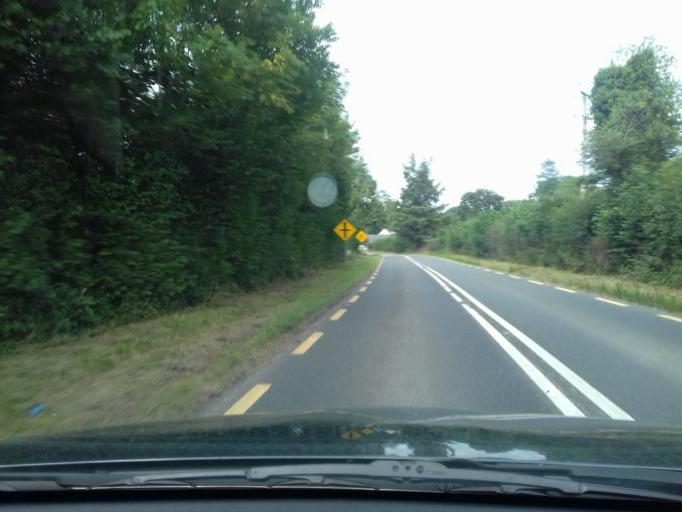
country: IE
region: Leinster
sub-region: Wicklow
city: Baltinglass
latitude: 52.9643
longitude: -6.6954
